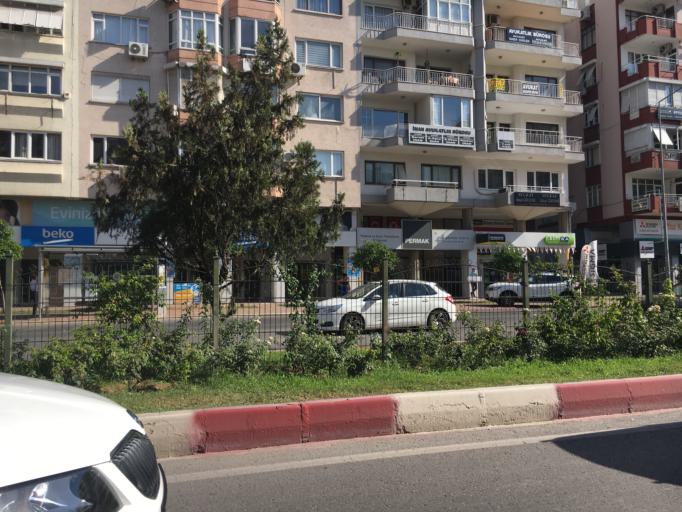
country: TR
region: Antalya
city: Antalya
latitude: 36.8903
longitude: 30.6905
